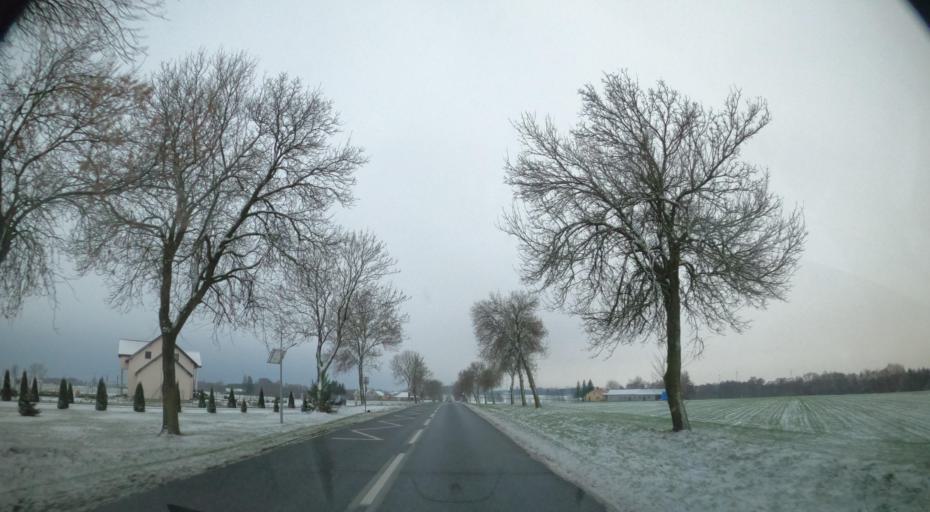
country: PL
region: Kujawsko-Pomorskie
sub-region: Powiat lipnowski
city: Dobrzyn nad Wisla
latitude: 52.6560
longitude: 19.3950
